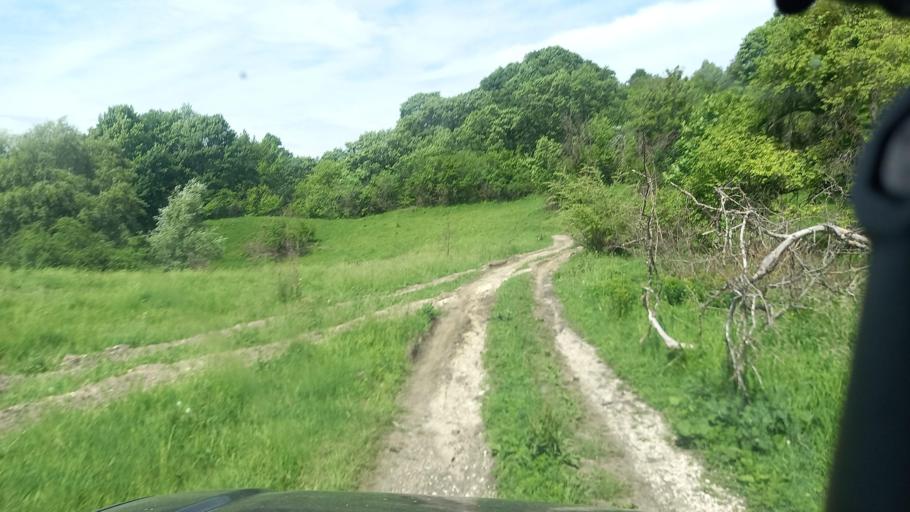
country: RU
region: Karachayevo-Cherkesiya
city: Kurdzhinovo
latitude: 44.1488
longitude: 41.0634
